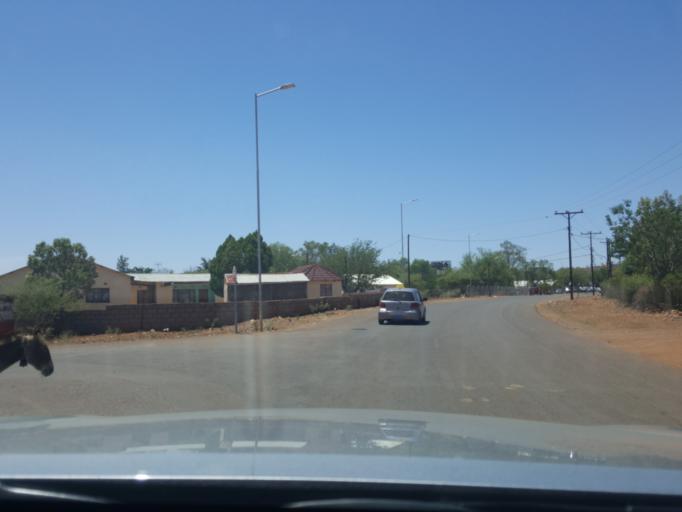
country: BW
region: South East
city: Ramotswa
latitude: -24.8707
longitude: 25.8793
